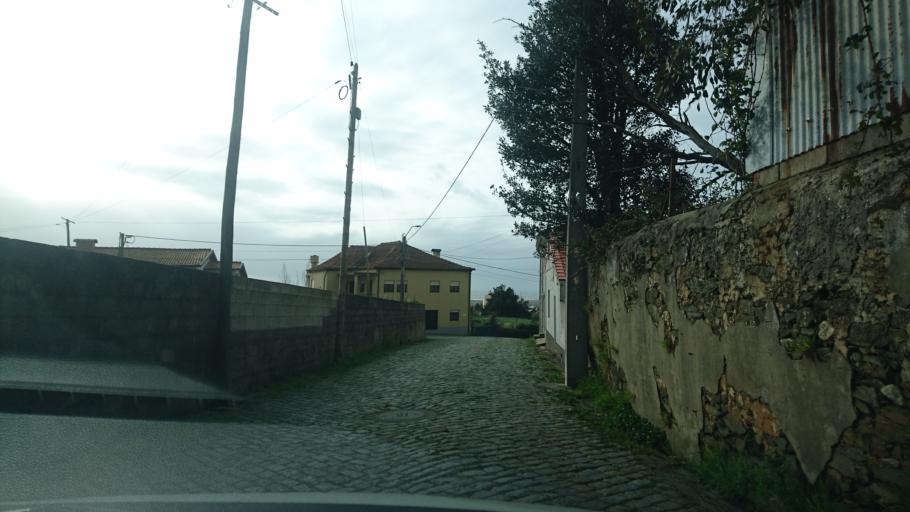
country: PT
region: Aveiro
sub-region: Ovar
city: Esmoriz
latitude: 40.9581
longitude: -8.6217
